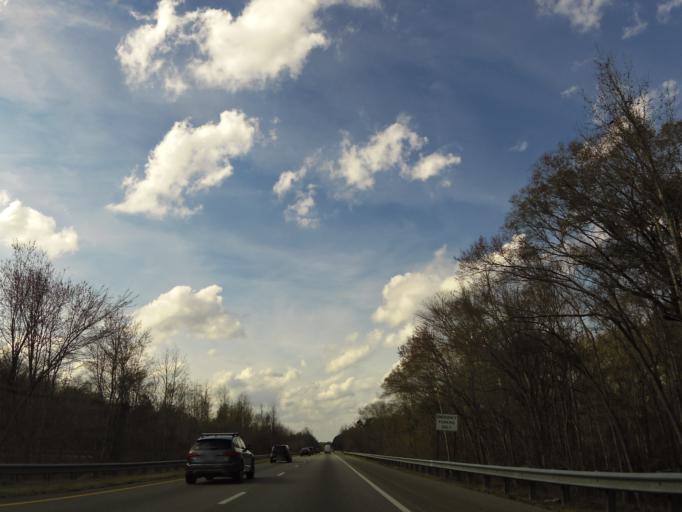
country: US
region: South Carolina
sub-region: Dorchester County
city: Ridgeville
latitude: 33.1459
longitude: -80.3282
